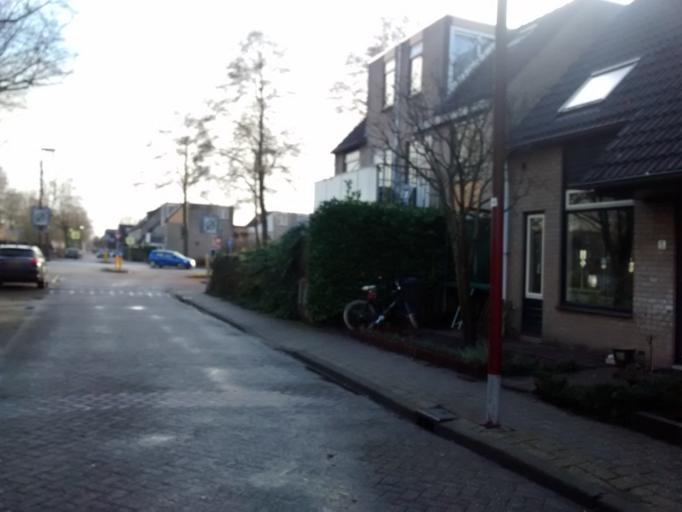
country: NL
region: Utrecht
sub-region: Gemeente Nieuwegein
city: Nieuwegein
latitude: 52.0158
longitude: 5.0907
